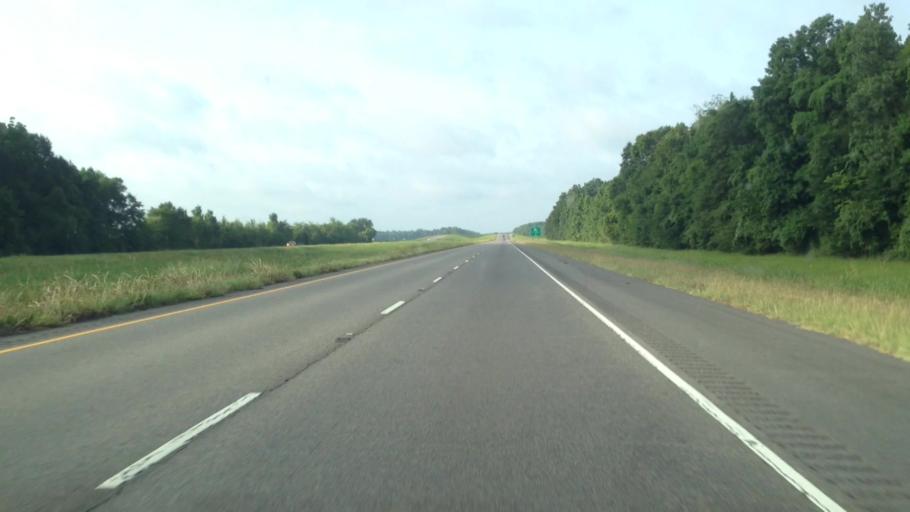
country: US
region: Louisiana
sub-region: Avoyelles Parish
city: Bunkie
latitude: 30.8753
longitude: -92.2279
